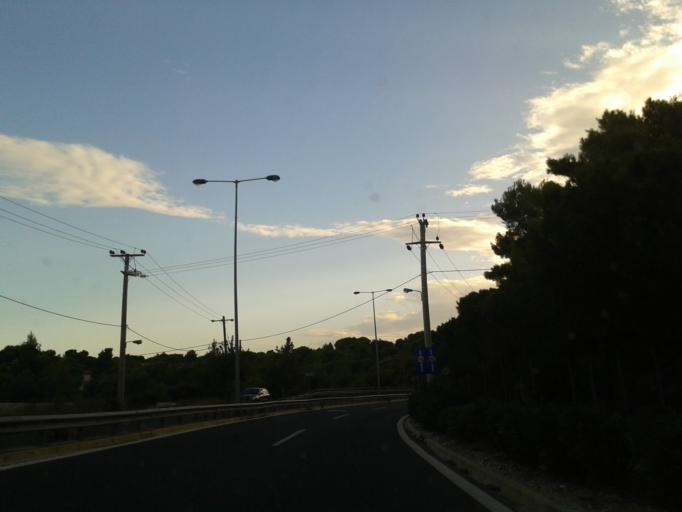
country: GR
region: Attica
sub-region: Nomarchia Anatolikis Attikis
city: Neos Voutzas
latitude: 38.0374
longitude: 23.9895
